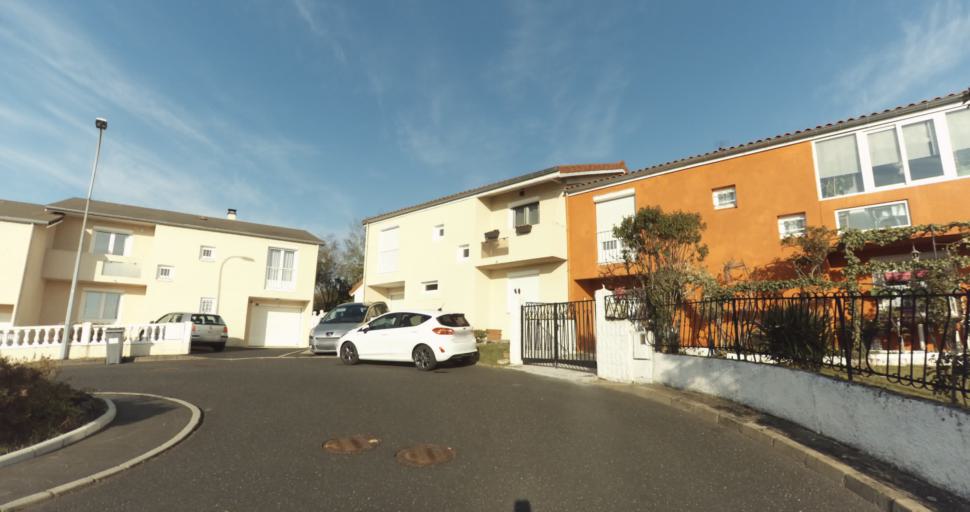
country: FR
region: Rhone-Alpes
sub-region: Departement de la Loire
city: Saint-Jean-Bonnefonds
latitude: 45.4505
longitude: 4.4396
